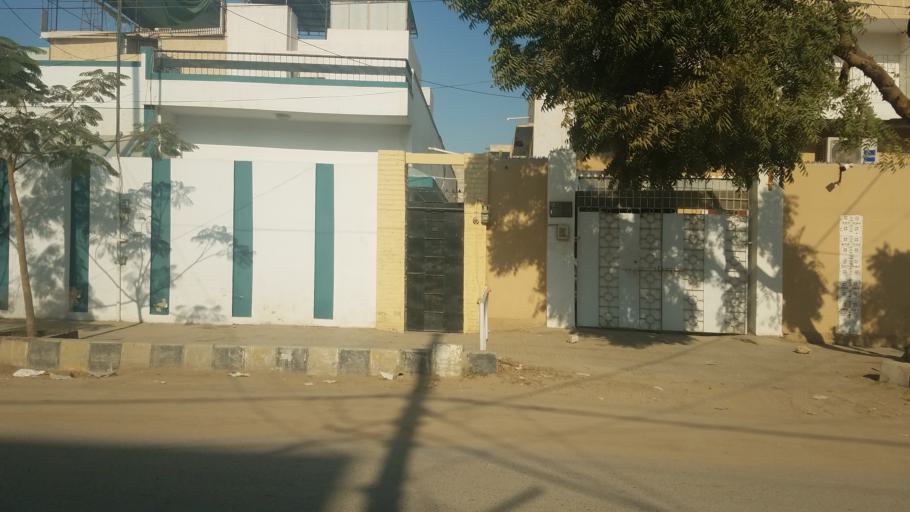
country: PK
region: Sindh
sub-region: Karachi District
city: Karachi
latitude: 24.9399
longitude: 67.0683
